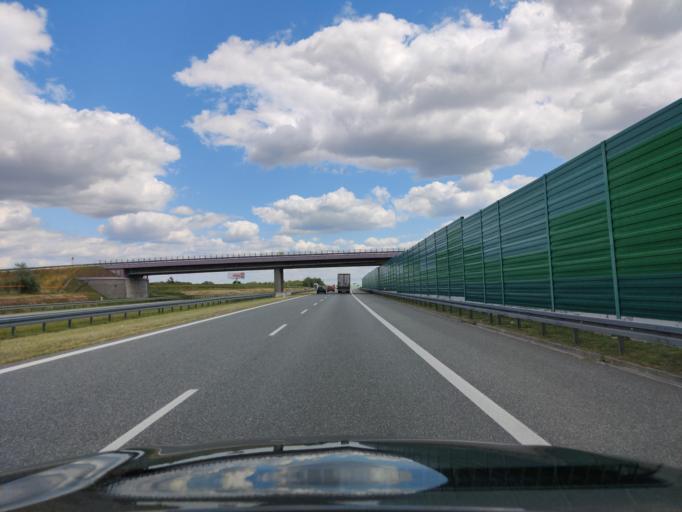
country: PL
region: Masovian Voivodeship
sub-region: Powiat minski
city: Ceglow
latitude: 52.2022
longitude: 21.7521
